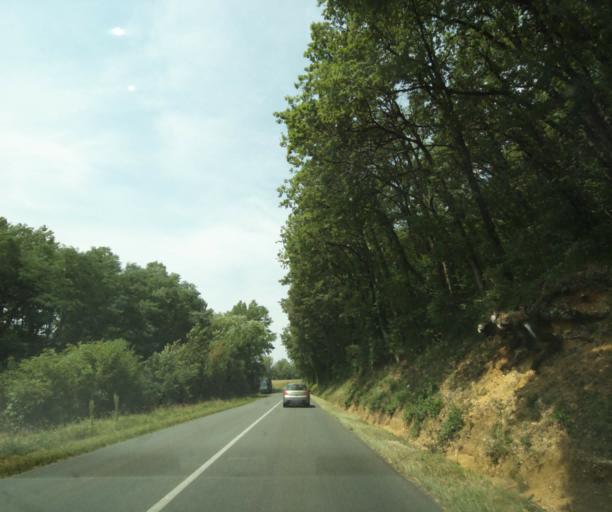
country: FR
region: Poitou-Charentes
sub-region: Departement de la Vienne
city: Lussac-les-Chateaux
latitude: 46.4145
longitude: 0.6986
